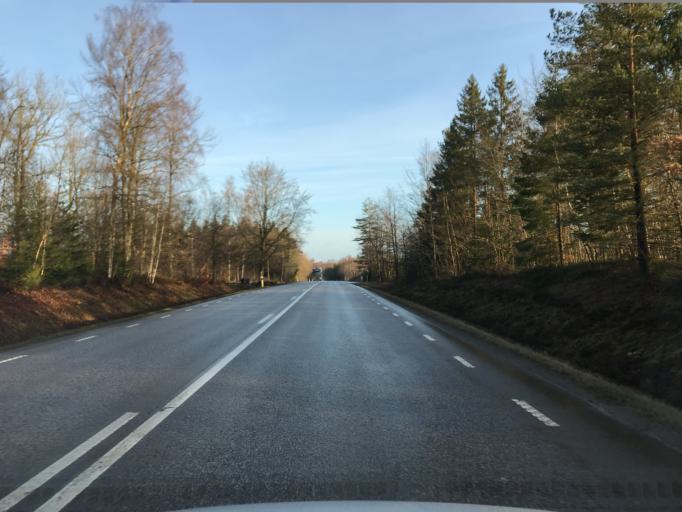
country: SE
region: Skane
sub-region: Hassleholms Kommun
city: Bjarnum
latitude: 56.2500
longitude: 13.7164
